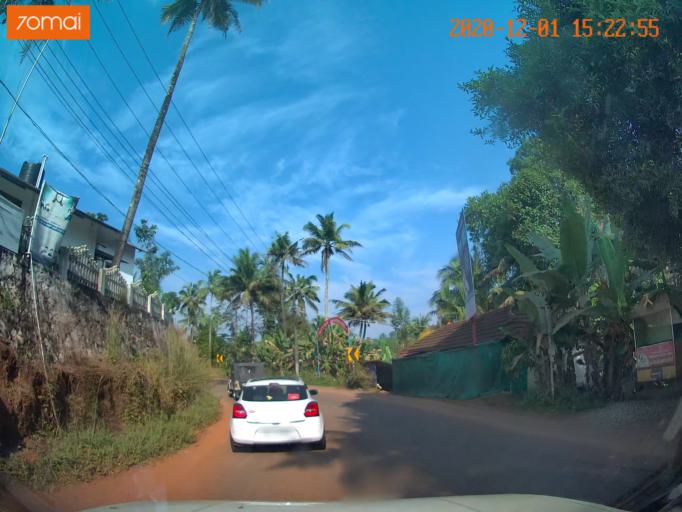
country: IN
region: Kerala
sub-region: Ernakulam
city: Muvattupuzha
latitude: 9.9486
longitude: 76.5498
